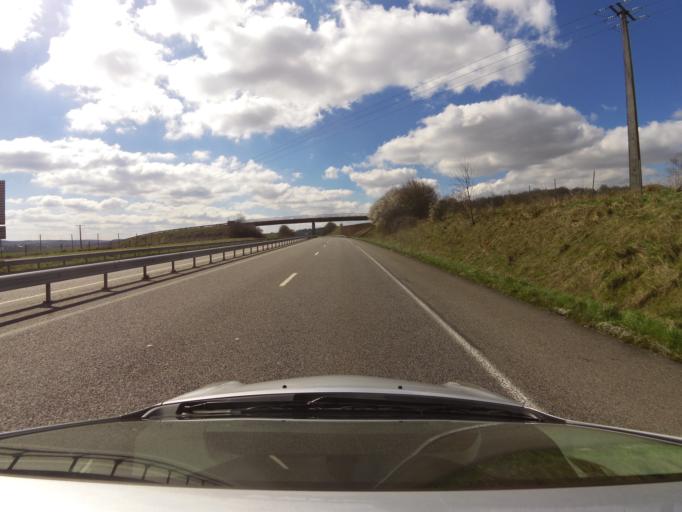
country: FR
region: Haute-Normandie
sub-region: Departement de la Seine-Maritime
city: Foucarmont
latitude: 49.8677
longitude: 1.5572
